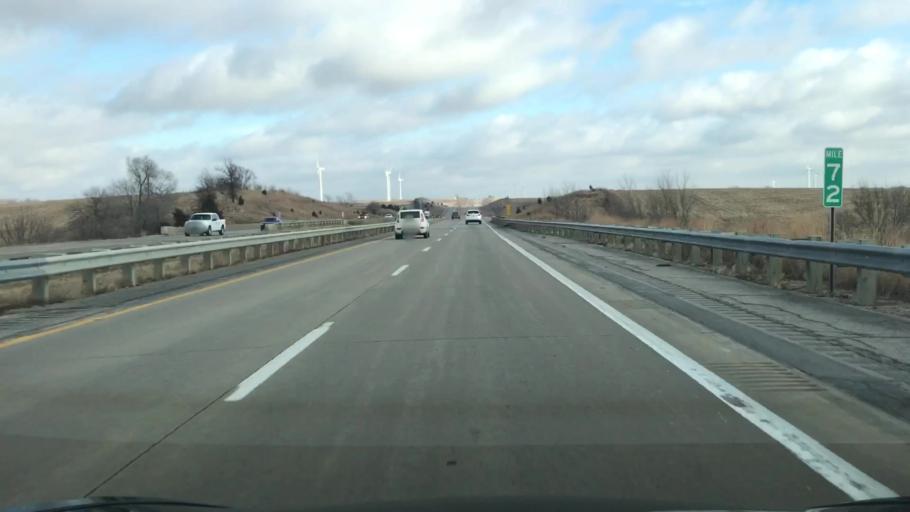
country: US
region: Iowa
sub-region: Guthrie County
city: Guthrie Center
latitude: 41.4966
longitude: -94.7257
